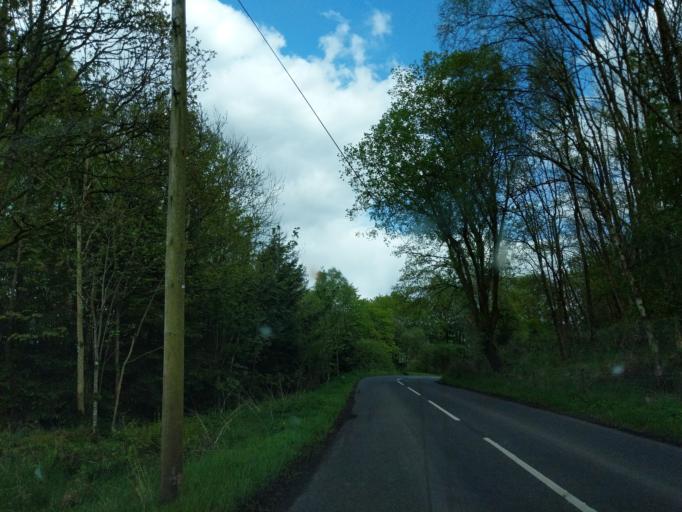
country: GB
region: Scotland
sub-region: Stirling
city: Balfron
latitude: 56.1342
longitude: -4.2458
